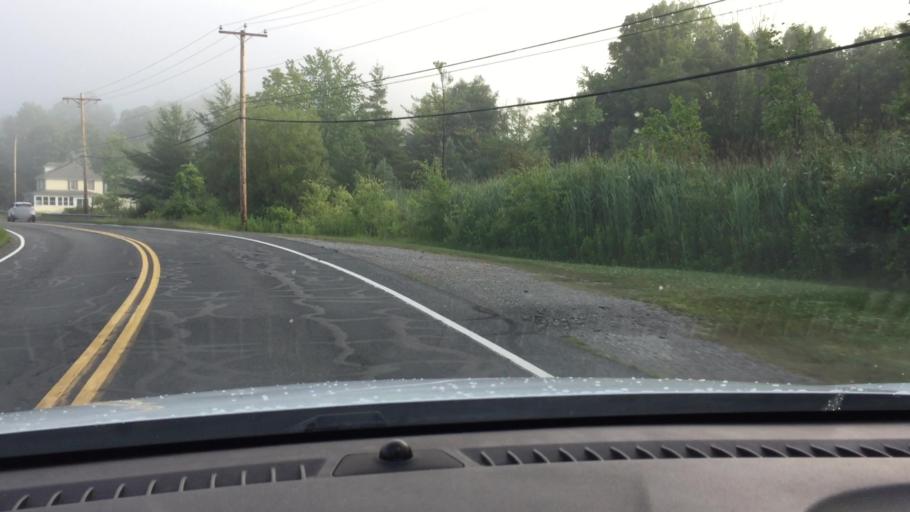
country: US
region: Massachusetts
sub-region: Berkshire County
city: Lee
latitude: 42.3261
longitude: -73.2402
